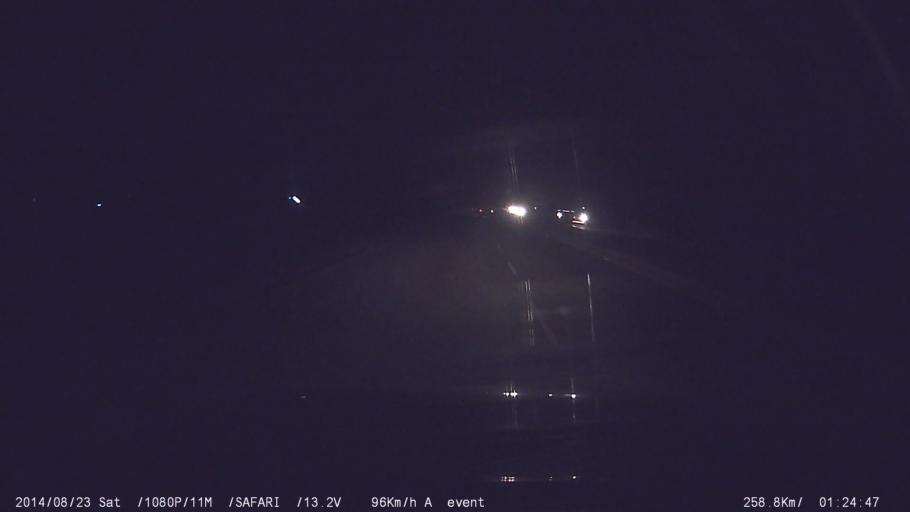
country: IN
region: Tamil Nadu
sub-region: Kancheepuram
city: Kanchipuram
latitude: 12.8712
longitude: 79.6542
